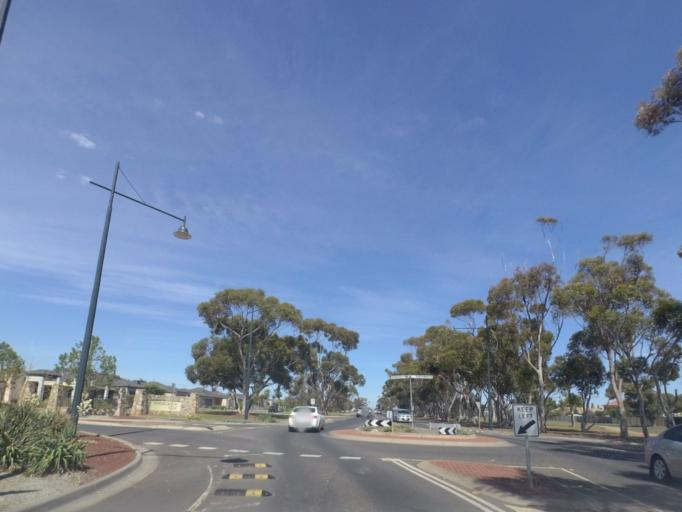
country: AU
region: Victoria
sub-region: Melton
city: Melton West
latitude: -37.6853
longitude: 144.5548
